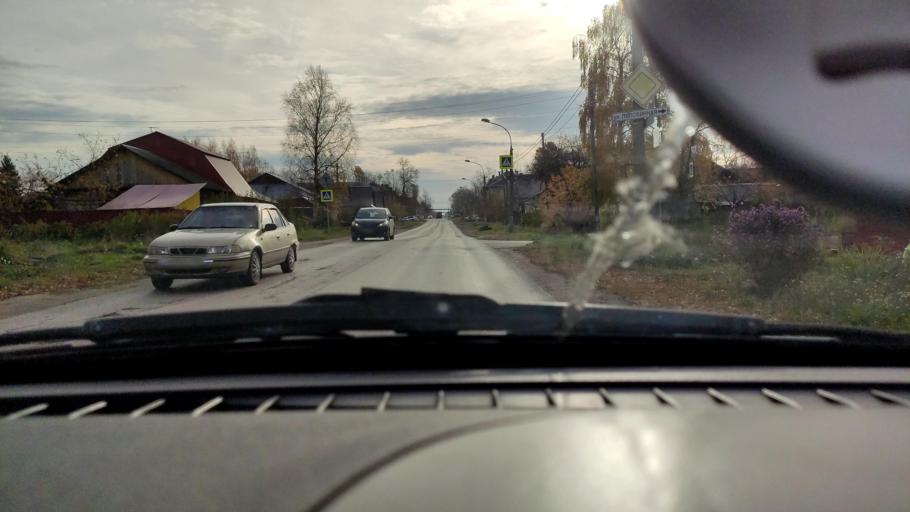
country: RU
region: Perm
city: Perm
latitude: 58.0907
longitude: 56.3877
